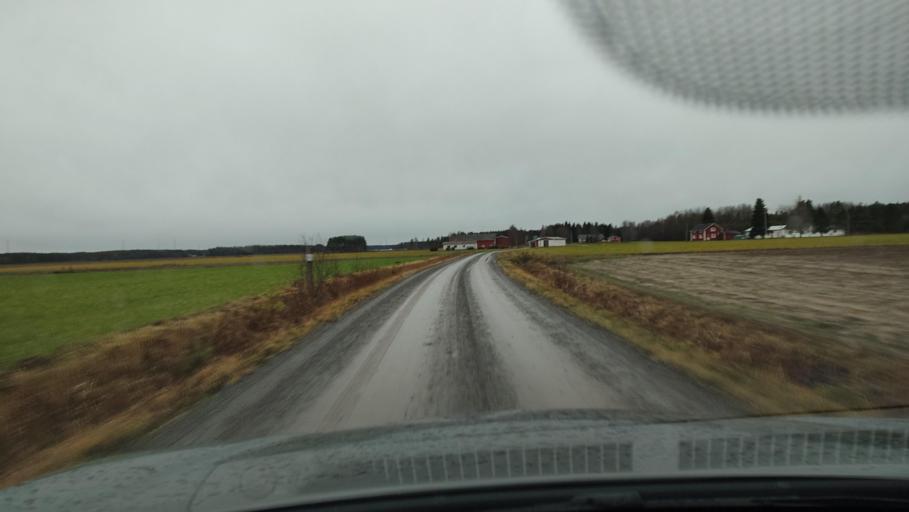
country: FI
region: Southern Ostrobothnia
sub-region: Suupohja
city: Karijoki
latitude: 62.2416
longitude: 21.5516
